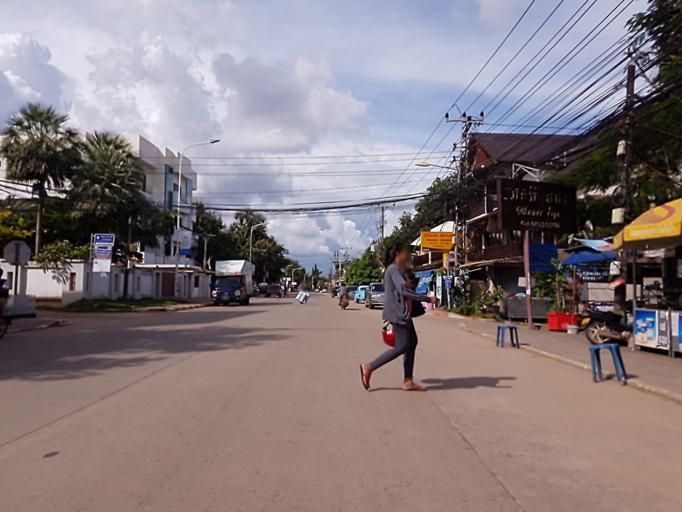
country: LA
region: Vientiane
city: Vientiane
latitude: 17.9349
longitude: 102.6252
